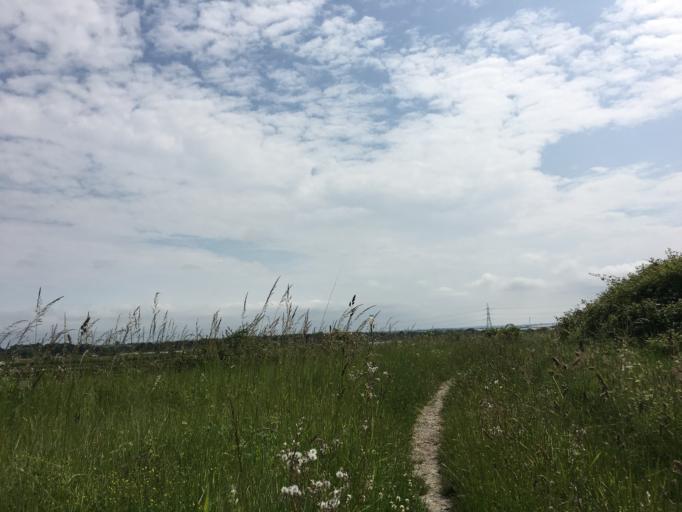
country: GB
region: England
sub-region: Kent
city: Sittingbourne
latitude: 51.3633
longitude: 0.7642
